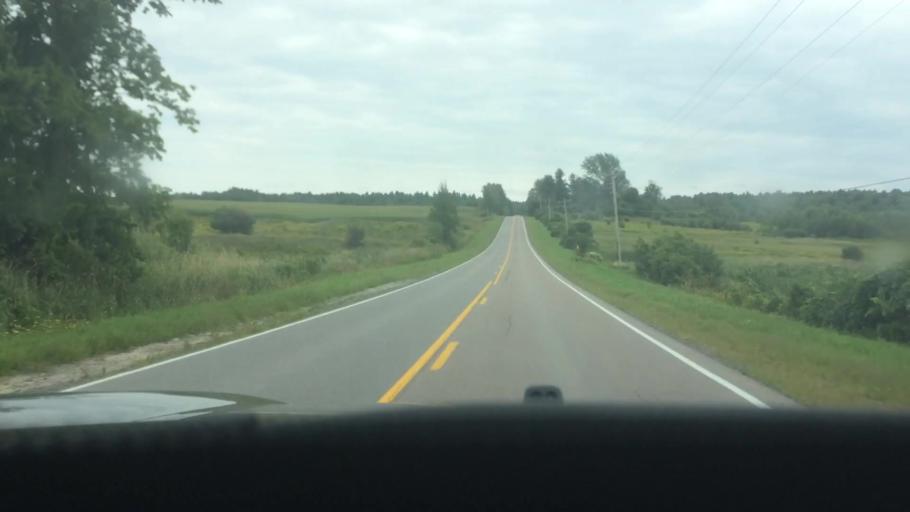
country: US
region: New York
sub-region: St. Lawrence County
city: Hannawa Falls
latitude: 44.5378
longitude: -75.0286
